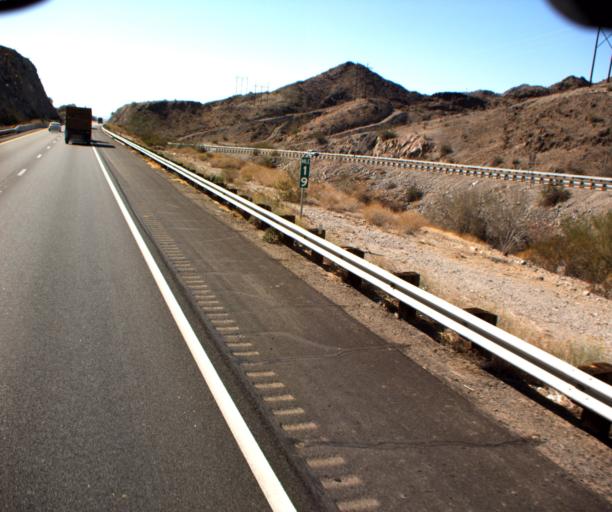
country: US
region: Arizona
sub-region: Yuma County
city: Fortuna Foothills
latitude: 32.6600
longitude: -114.3299
